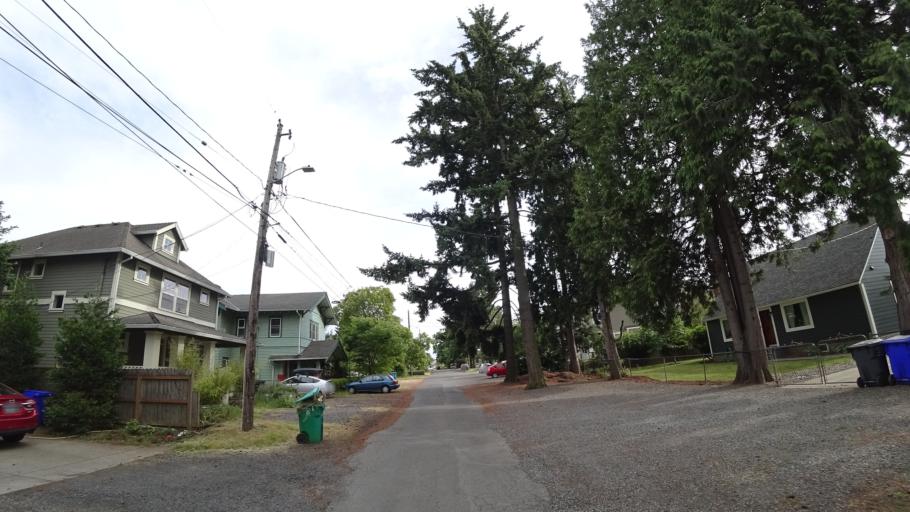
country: US
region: Oregon
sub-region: Multnomah County
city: Portland
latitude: 45.5733
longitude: -122.6898
